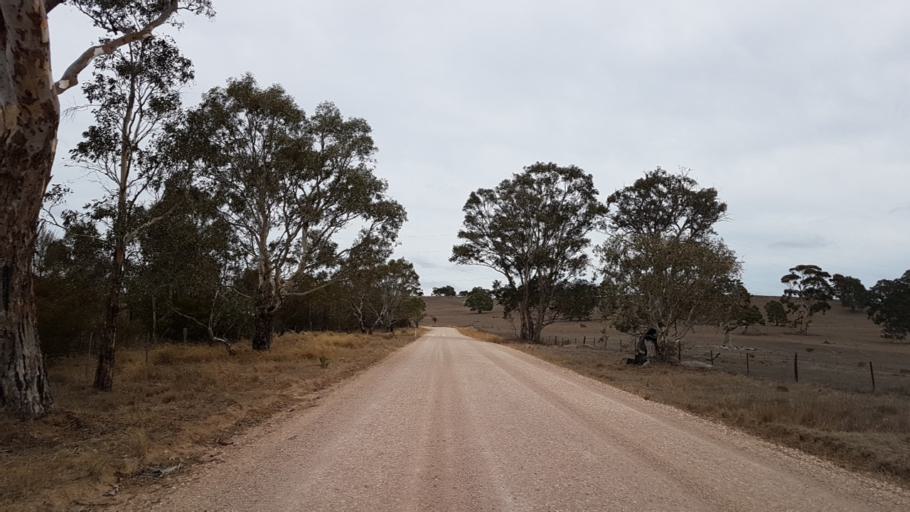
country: AU
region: South Australia
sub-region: Adelaide Hills
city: Birdwood
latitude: -34.8860
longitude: 139.0761
